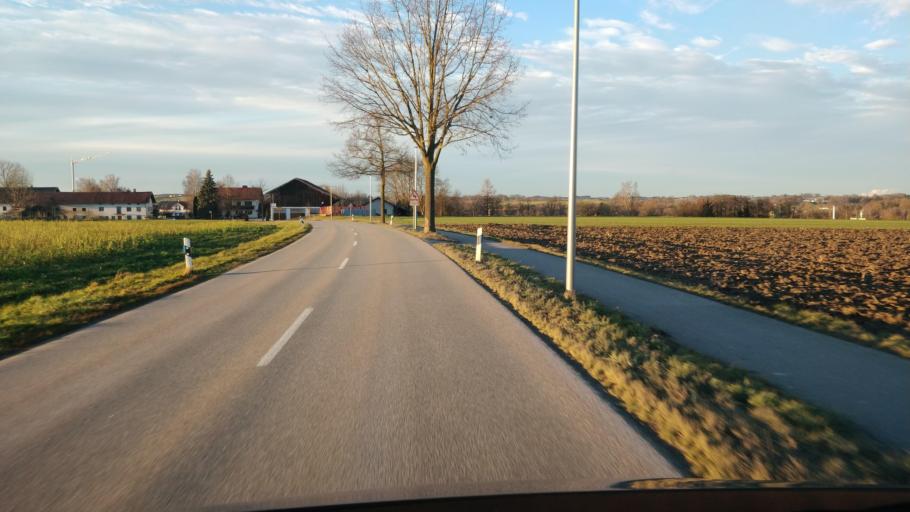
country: DE
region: Bavaria
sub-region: Upper Bavaria
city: Obertaufkirchen
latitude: 48.2680
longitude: 12.2726
